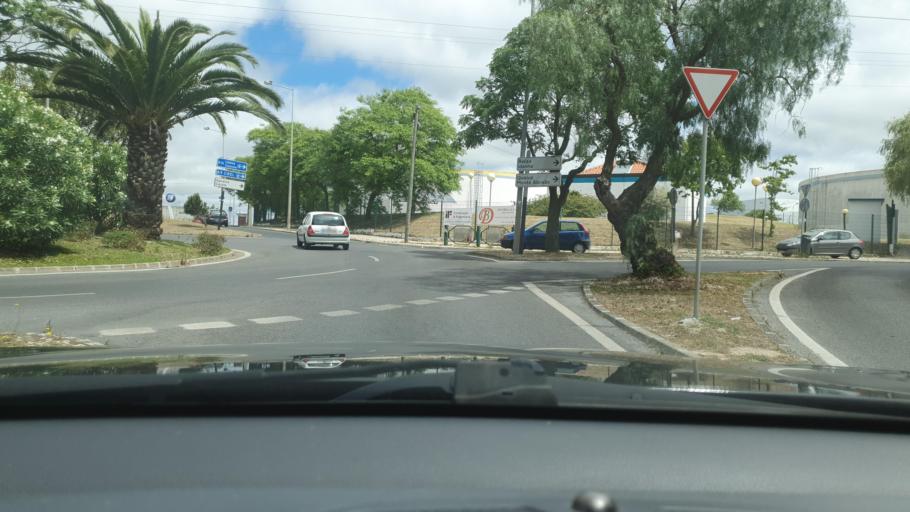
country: PT
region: Lisbon
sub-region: Sintra
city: Cacem
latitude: 38.7655
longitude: -9.2790
